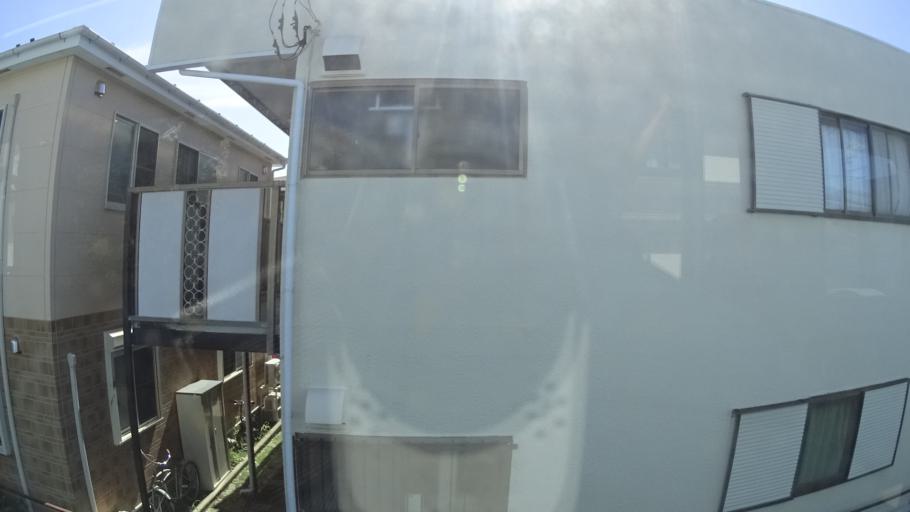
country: JP
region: Kanagawa
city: Fujisawa
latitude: 35.3313
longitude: 139.4854
